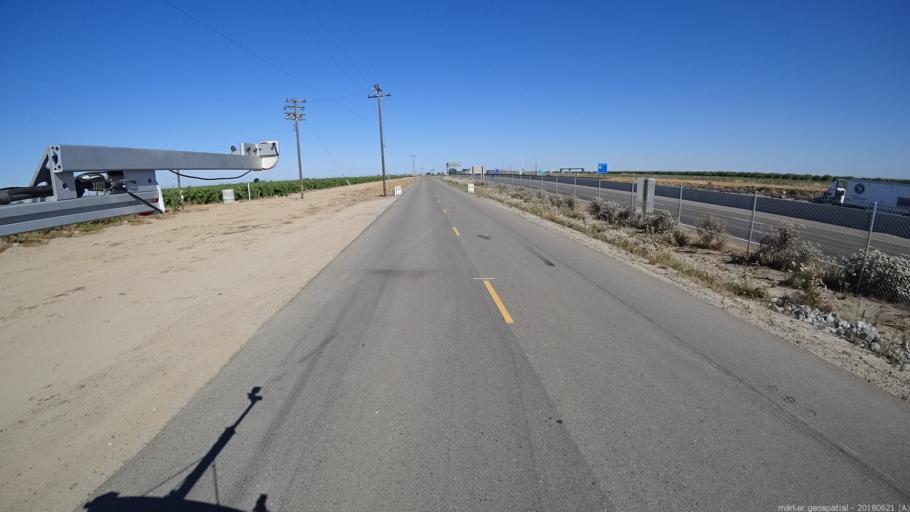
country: US
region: California
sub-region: Fresno County
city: Biola
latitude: 36.8451
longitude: -119.9372
